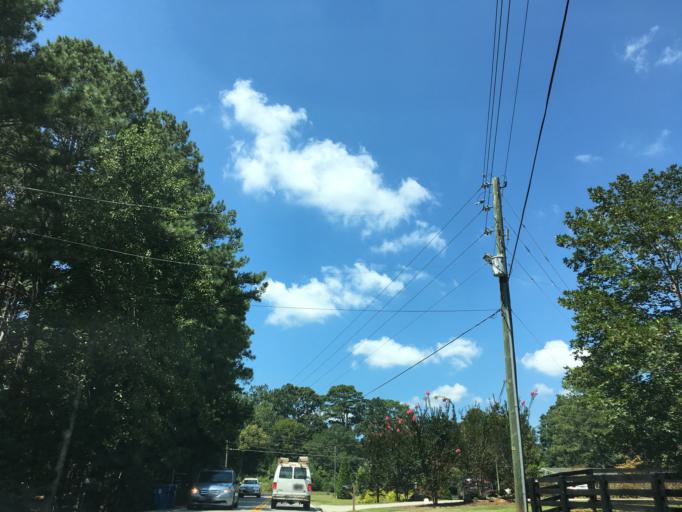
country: US
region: Georgia
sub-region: Fulton County
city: Milton
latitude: 34.1176
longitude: -84.3055
